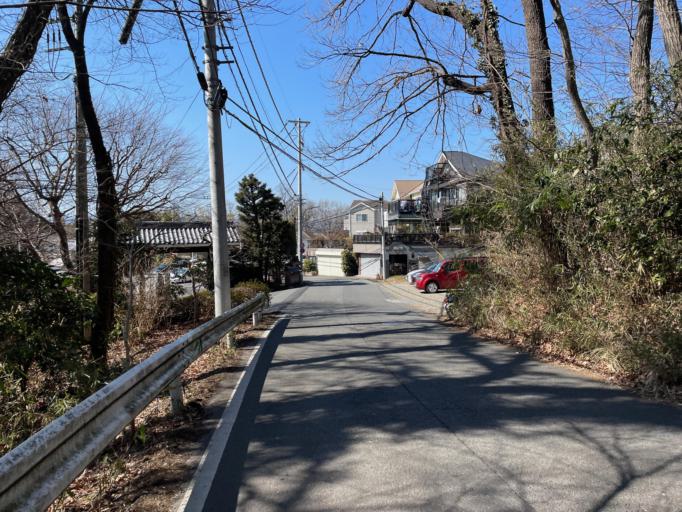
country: JP
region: Tokyo
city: Hachioji
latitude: 35.6735
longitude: 139.3354
